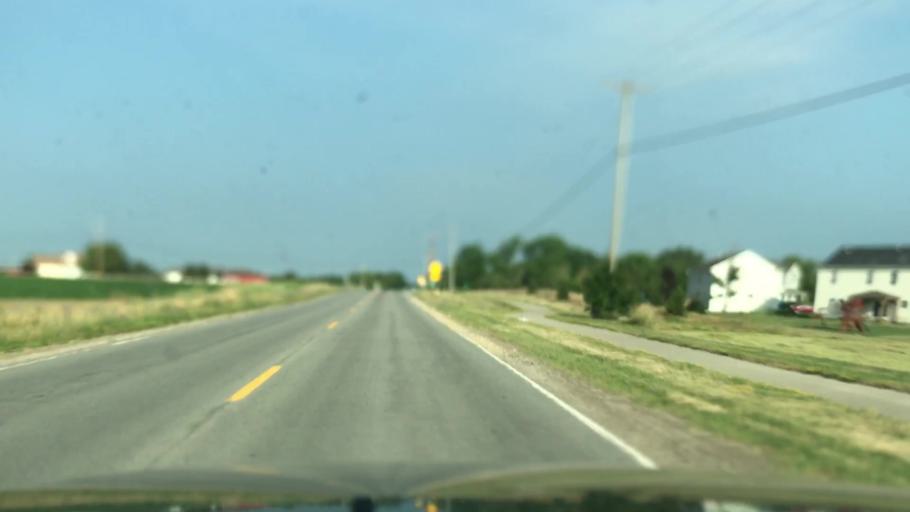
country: US
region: Michigan
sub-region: Ottawa County
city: Hudsonville
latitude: 42.8403
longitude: -85.8397
